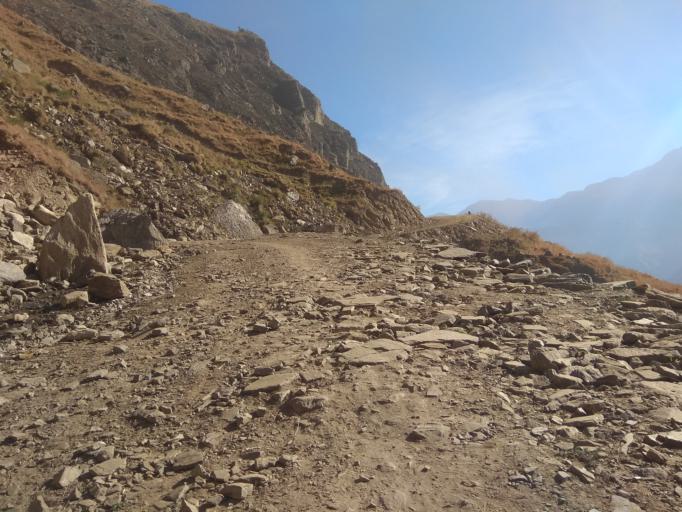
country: NP
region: Mid Western
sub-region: Bheri Zone
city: Dailekh
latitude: 29.2960
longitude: 81.7077
